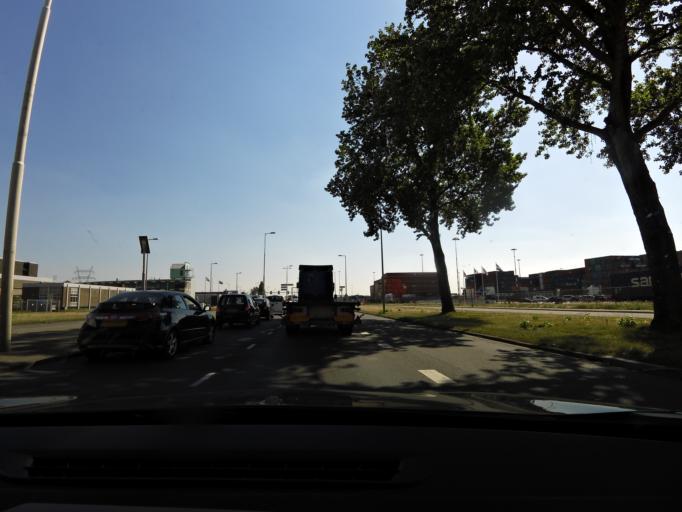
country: NL
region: South Holland
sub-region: Gemeente Albrandswaard
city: Rhoon
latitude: 51.8769
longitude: 4.4320
